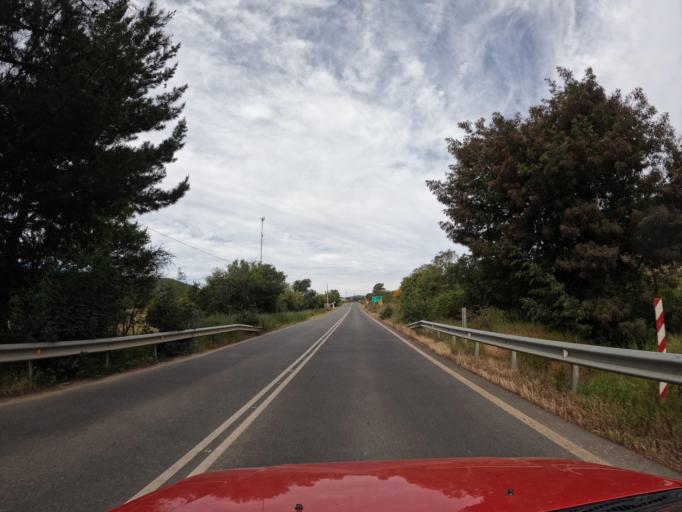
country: CL
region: Maule
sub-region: Provincia de Talca
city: Talca
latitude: -35.3228
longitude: -71.9363
